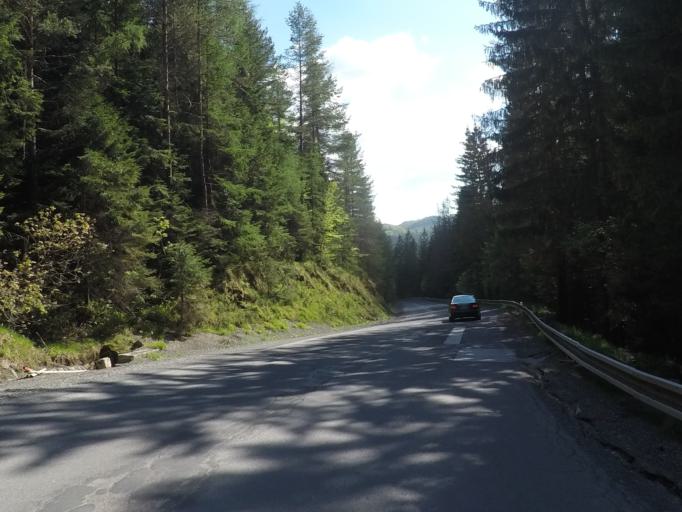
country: SK
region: Kosicky
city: Dobsina
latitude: 48.8899
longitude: 20.2411
